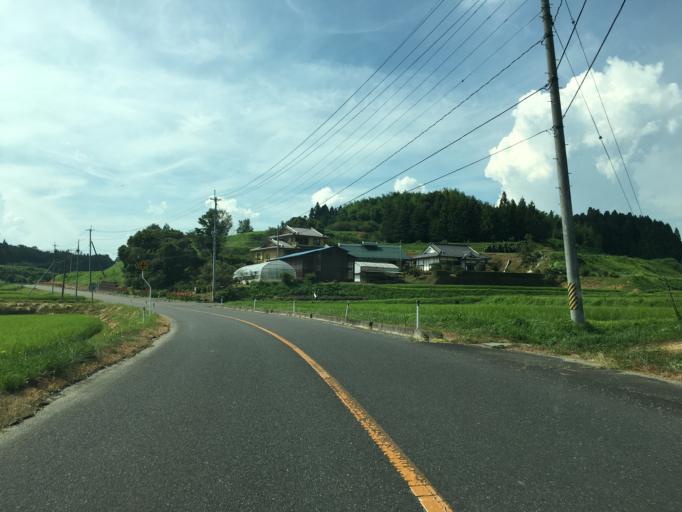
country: JP
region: Fukushima
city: Ishikawa
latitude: 37.2233
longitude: 140.4454
